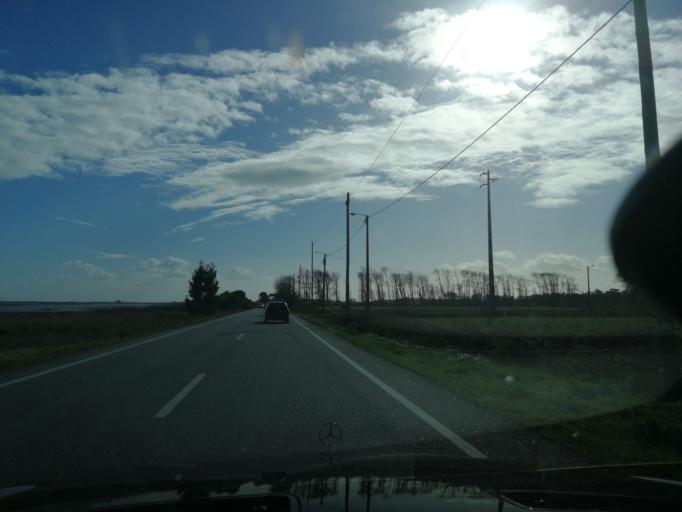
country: PT
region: Aveiro
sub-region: Estarreja
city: Pardilho
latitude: 40.8136
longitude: -8.6708
